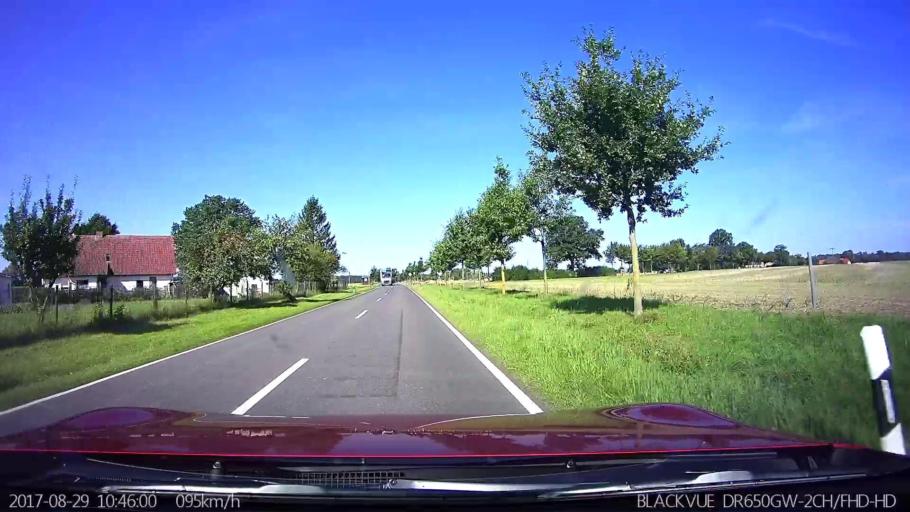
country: DE
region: Mecklenburg-Vorpommern
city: Franzburg
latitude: 54.2189
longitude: 12.8517
